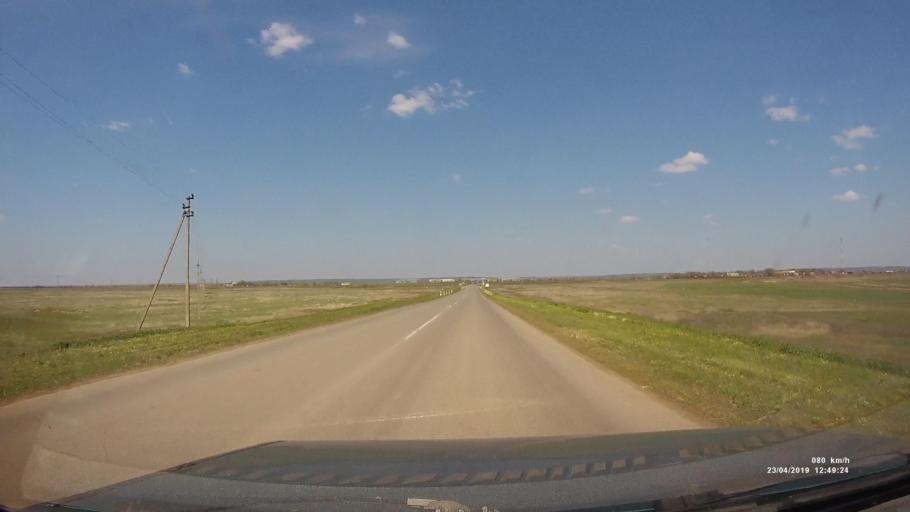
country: RU
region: Kalmykiya
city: Yashalta
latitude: 46.5367
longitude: 42.6392
